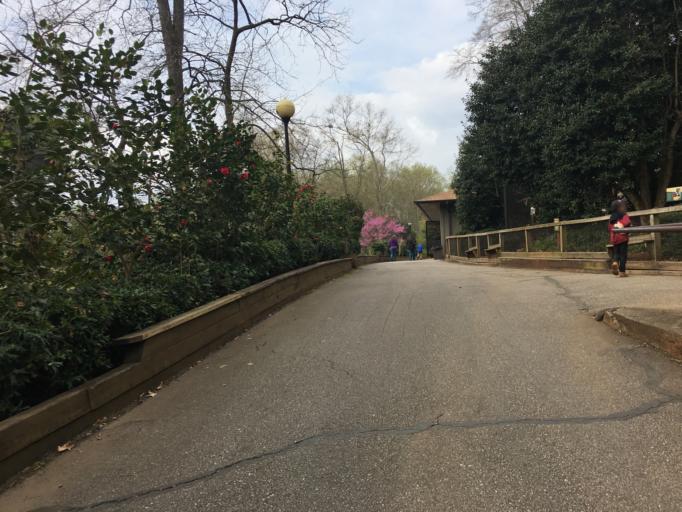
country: US
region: South Carolina
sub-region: Greenville County
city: Greenville
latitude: 34.8468
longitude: -82.3870
